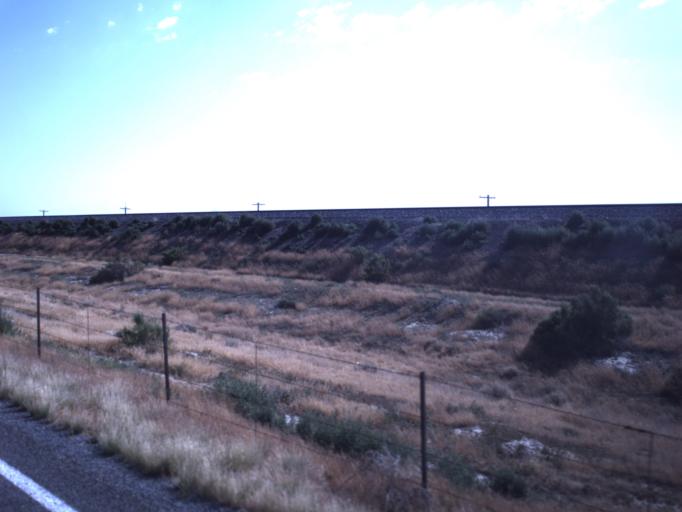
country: US
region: Utah
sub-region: Millard County
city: Delta
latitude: 38.9674
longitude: -112.8005
